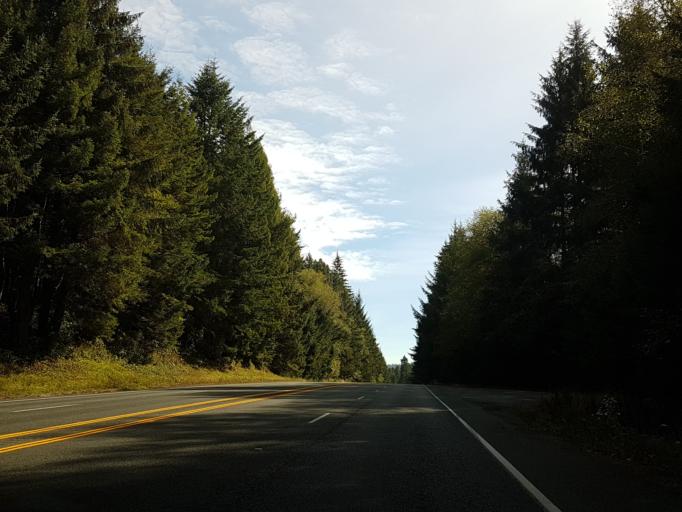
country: US
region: California
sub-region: Del Norte County
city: Bertsch-Oceanview
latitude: 41.4828
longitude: -124.0504
